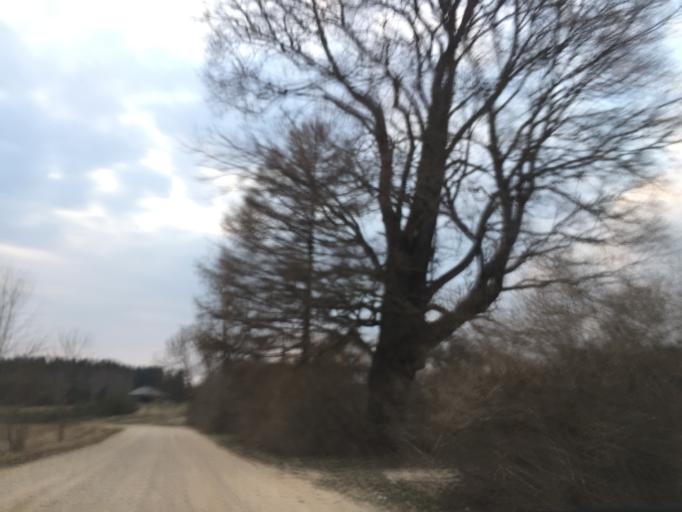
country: LV
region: Raunas
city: Rauna
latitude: 57.1405
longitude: 25.6156
